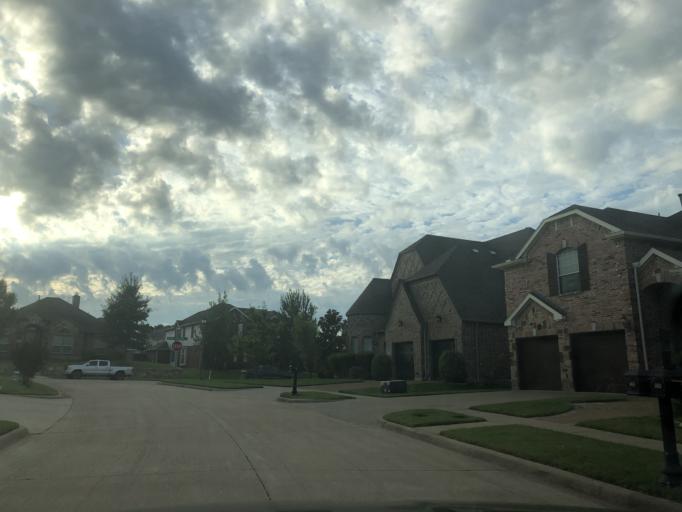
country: US
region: Texas
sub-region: Dallas County
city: Rowlett
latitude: 32.8498
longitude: -96.5892
